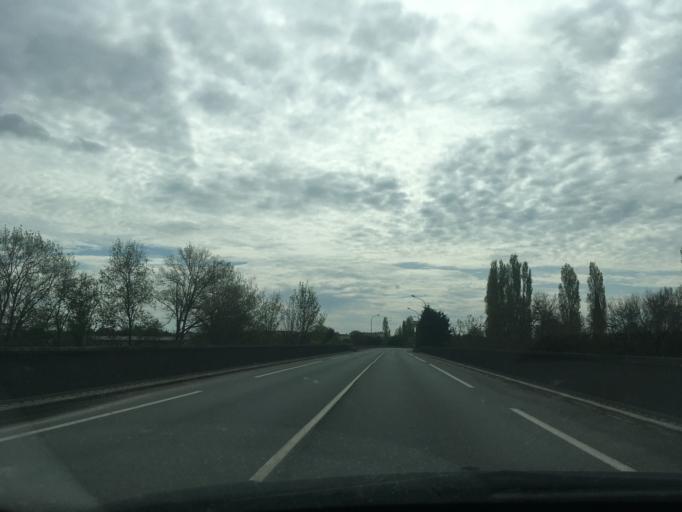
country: FR
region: Poitou-Charentes
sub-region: Departement de la Charente
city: Cognac
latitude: 45.6872
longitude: -0.3427
